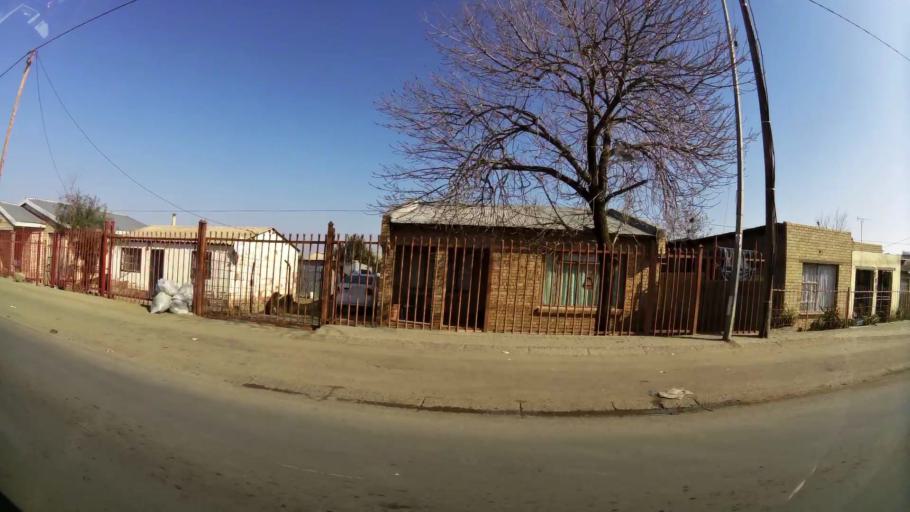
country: ZA
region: Orange Free State
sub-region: Mangaung Metropolitan Municipality
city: Bloemfontein
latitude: -29.1665
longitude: 26.2368
